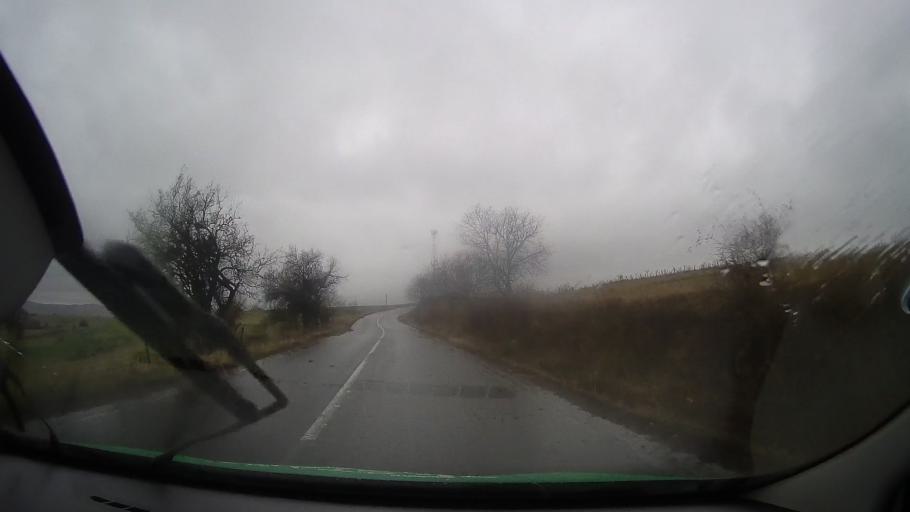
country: RO
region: Mures
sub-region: Comuna Vatava
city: Vatava
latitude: 46.9571
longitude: 24.7542
